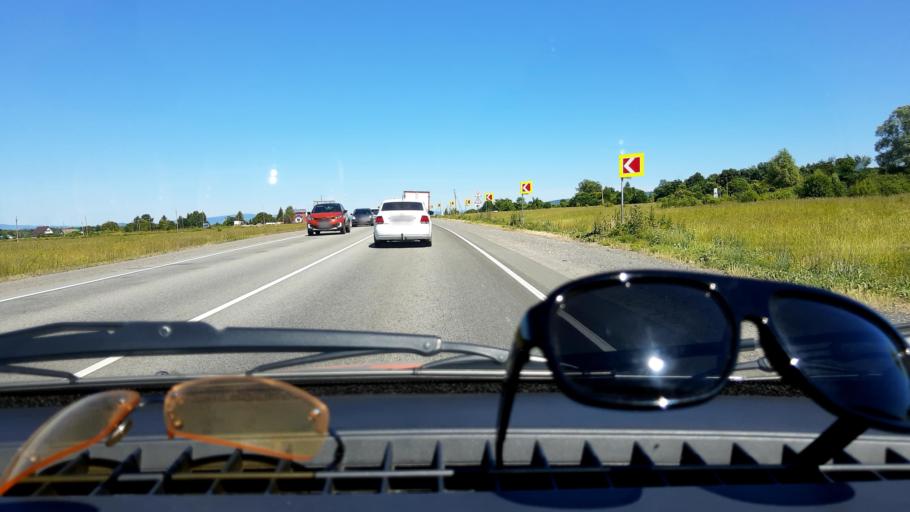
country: RU
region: Bashkortostan
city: Urman
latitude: 54.8180
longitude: 56.8718
